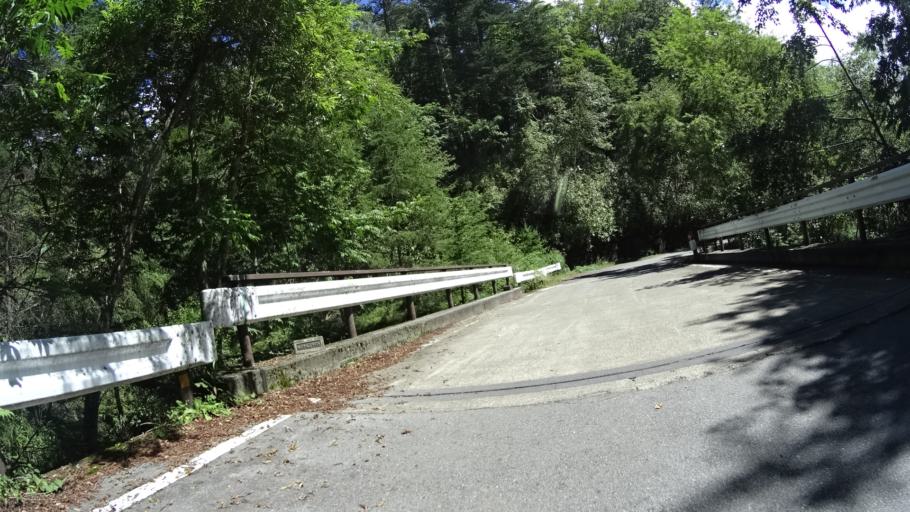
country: JP
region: Yamanashi
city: Enzan
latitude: 35.7335
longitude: 138.8402
